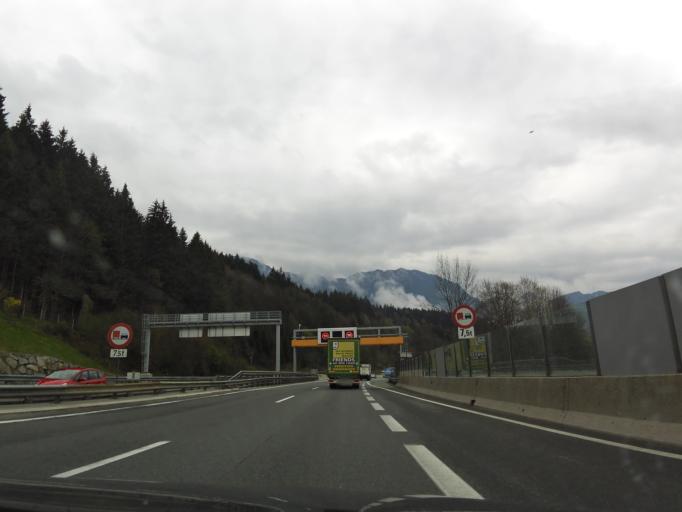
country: AT
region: Tyrol
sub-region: Politischer Bezirk Kufstein
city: Angath
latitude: 47.5005
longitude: 12.0582
